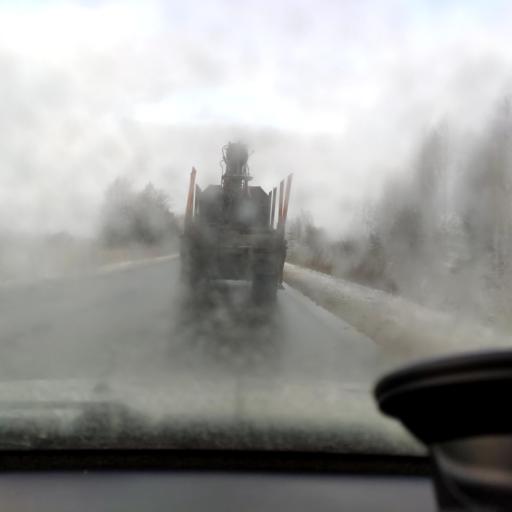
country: RU
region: Perm
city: Nytva
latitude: 57.9392
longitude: 55.3722
